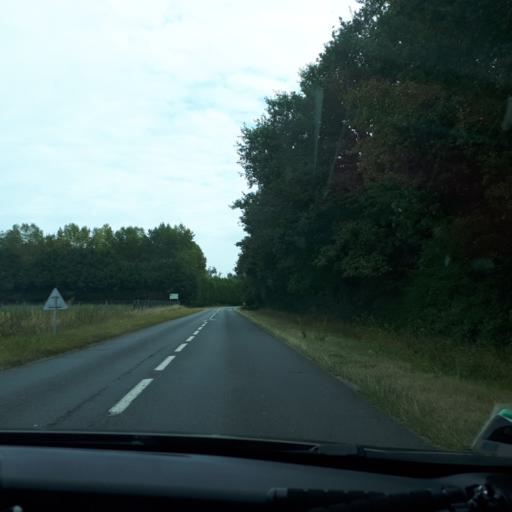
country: FR
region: Centre
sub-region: Departement du Loiret
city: Ouzouer-sur-Loire
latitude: 47.7688
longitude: 2.4594
